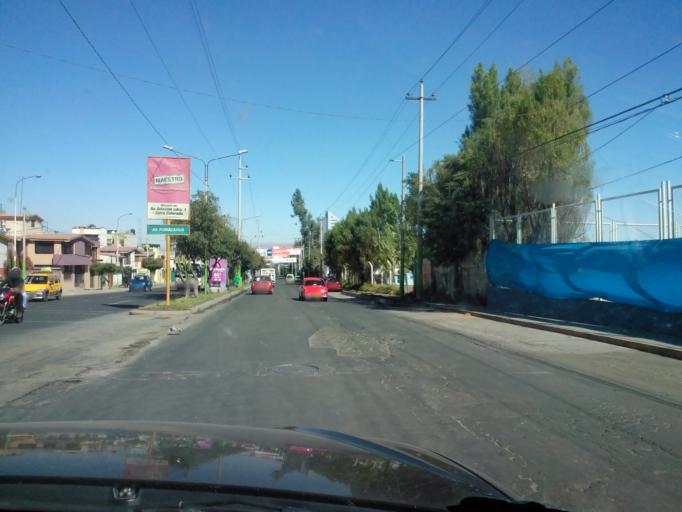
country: PE
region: Arequipa
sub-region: Provincia de Arequipa
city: Arequipa
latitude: -16.3811
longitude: -71.5567
